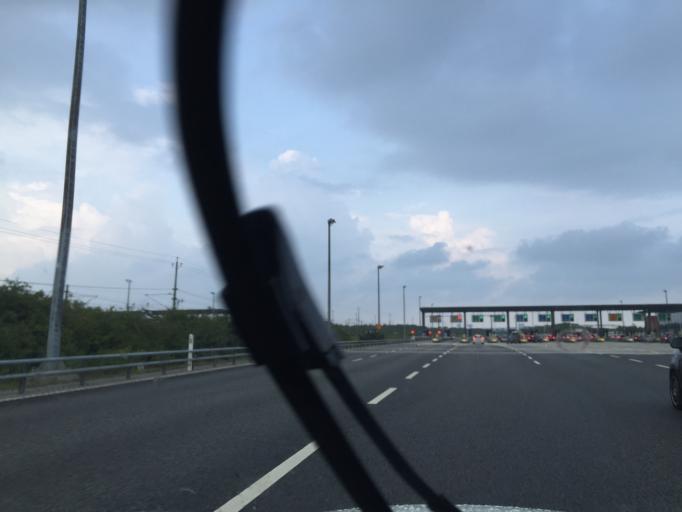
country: SE
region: Skane
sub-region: Malmo
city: Bunkeflostrand
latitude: 55.5649
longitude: 12.9102
